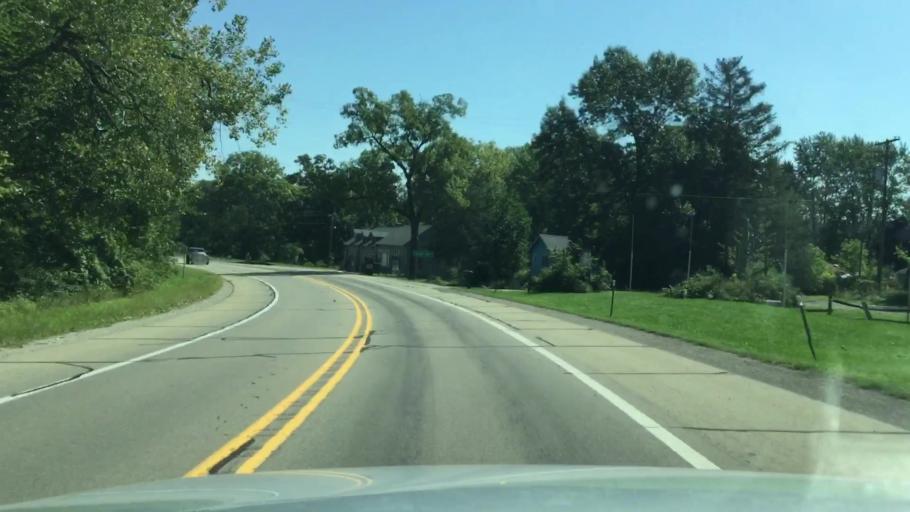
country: US
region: Michigan
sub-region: Jackson County
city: Brooklyn
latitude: 42.0564
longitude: -84.1489
